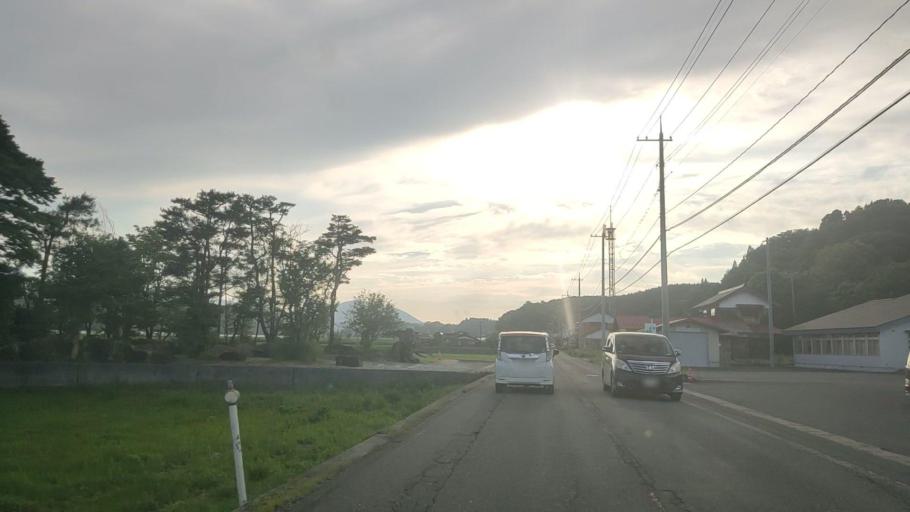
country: JP
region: Tottori
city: Kurayoshi
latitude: 35.2799
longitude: 133.6725
